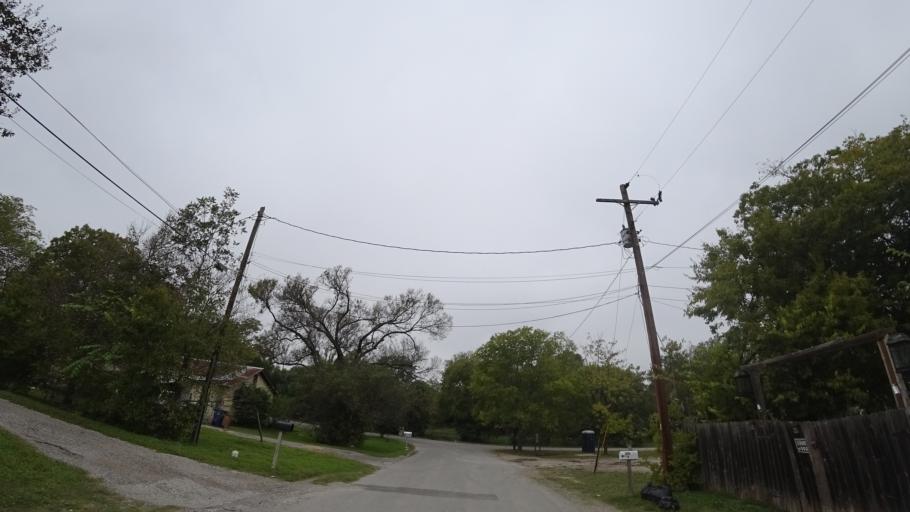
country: US
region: Texas
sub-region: Travis County
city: Austin
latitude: 30.2080
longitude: -97.7774
